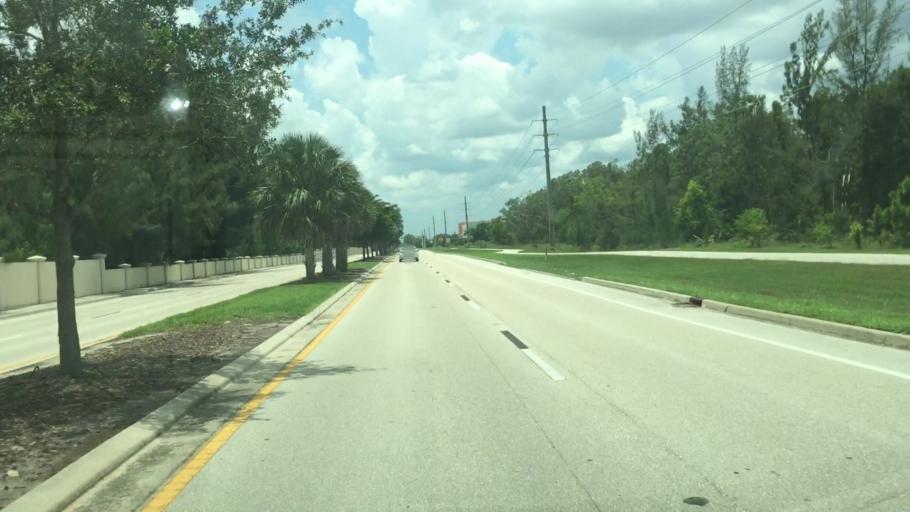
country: US
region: Florida
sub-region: Lee County
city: Pine Manor
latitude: 26.5874
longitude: -81.8475
